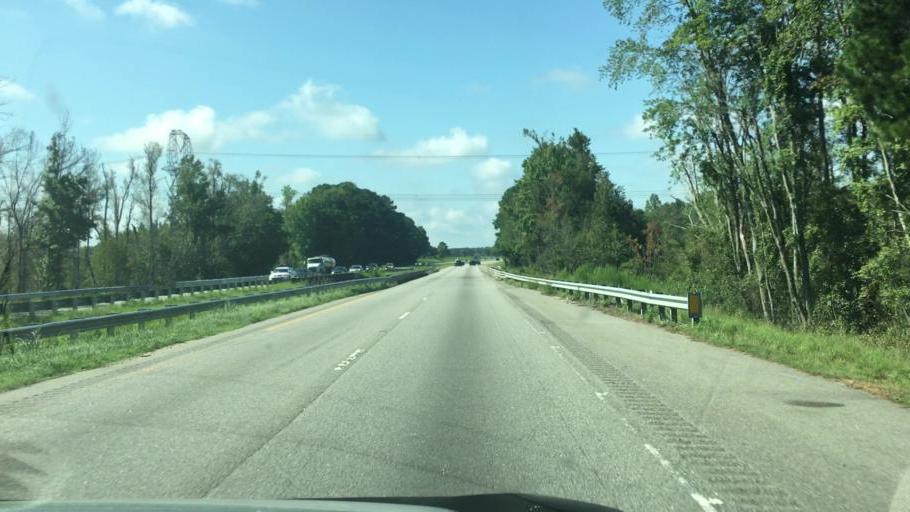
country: US
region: North Carolina
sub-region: Robeson County
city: Saint Pauls
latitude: 34.8595
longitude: -78.9657
